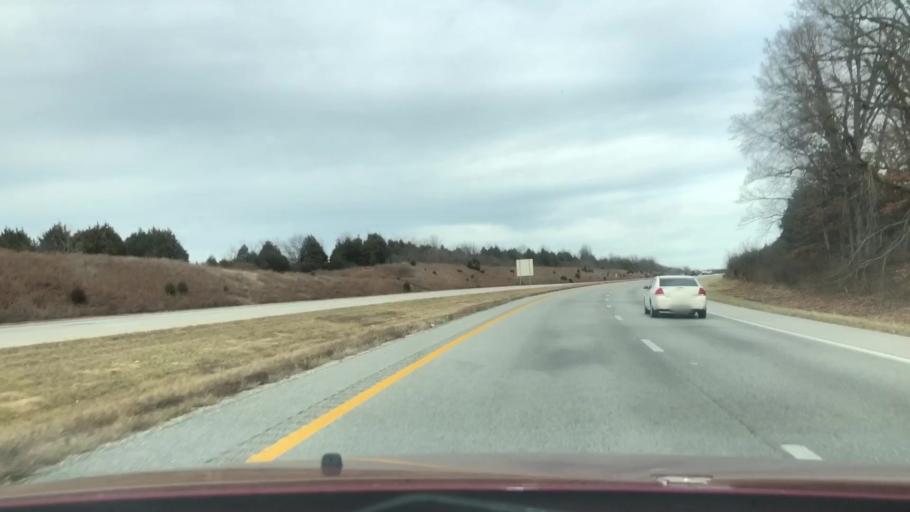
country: US
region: Missouri
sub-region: Greene County
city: Springfield
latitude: 37.2662
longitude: -93.2232
